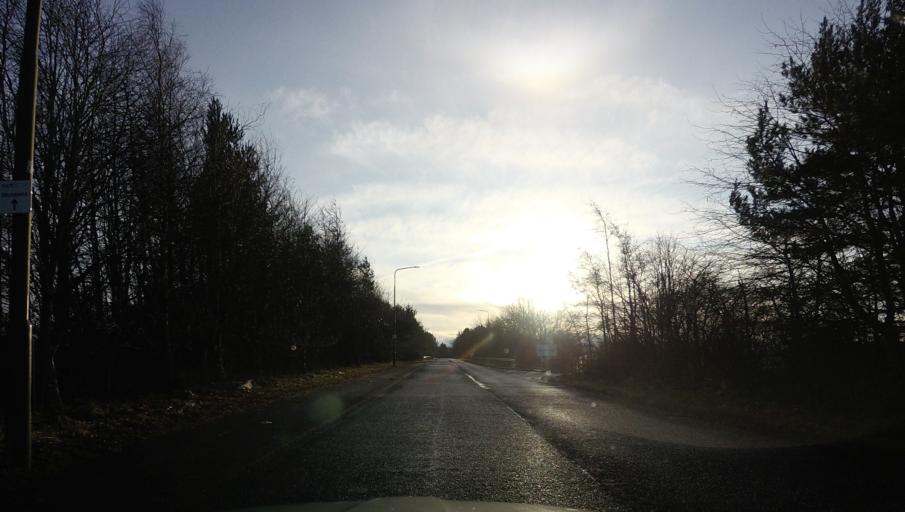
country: GB
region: Scotland
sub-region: West Lothian
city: Mid Calder
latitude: 55.8760
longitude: -3.4868
